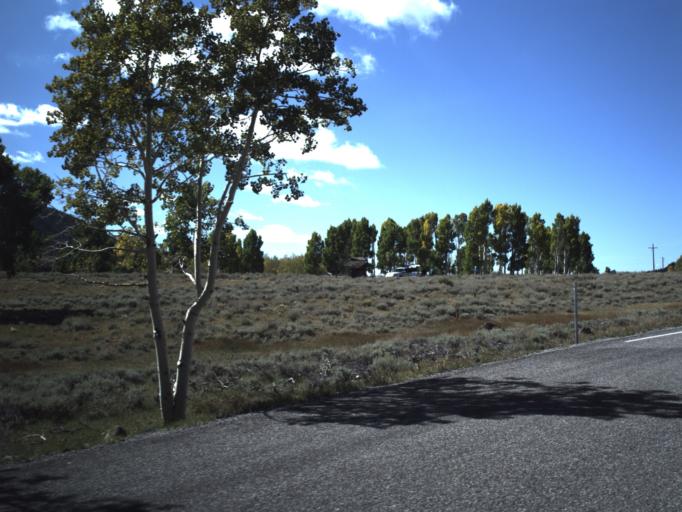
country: US
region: Utah
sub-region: Wayne County
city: Loa
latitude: 38.5309
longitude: -111.7417
